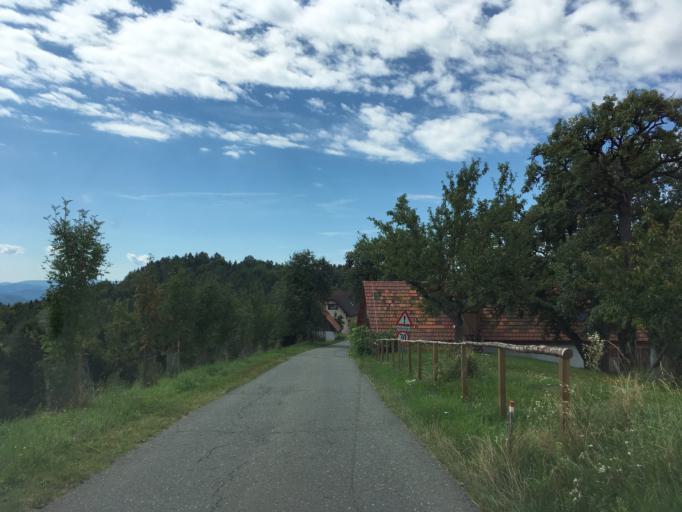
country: AT
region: Styria
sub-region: Politischer Bezirk Leibnitz
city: Kitzeck im Sausal
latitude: 46.7875
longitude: 15.4224
